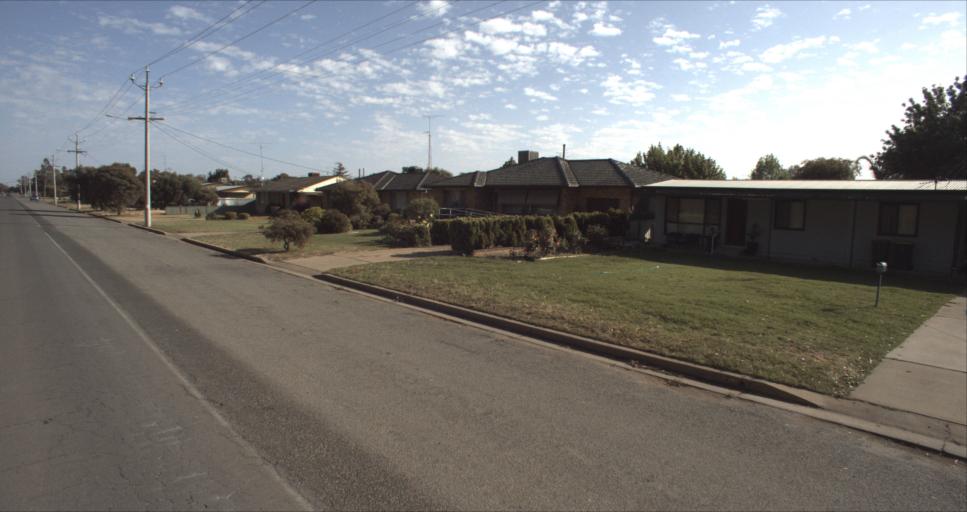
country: AU
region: New South Wales
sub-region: Leeton
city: Leeton
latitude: -34.5557
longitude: 146.3886
